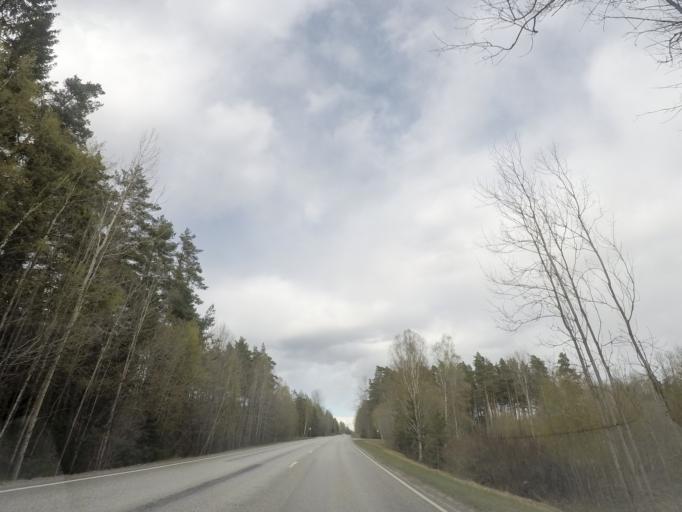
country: SE
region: Vaestmanland
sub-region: Kungsors Kommun
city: Kungsoer
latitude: 59.3009
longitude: 16.2193
